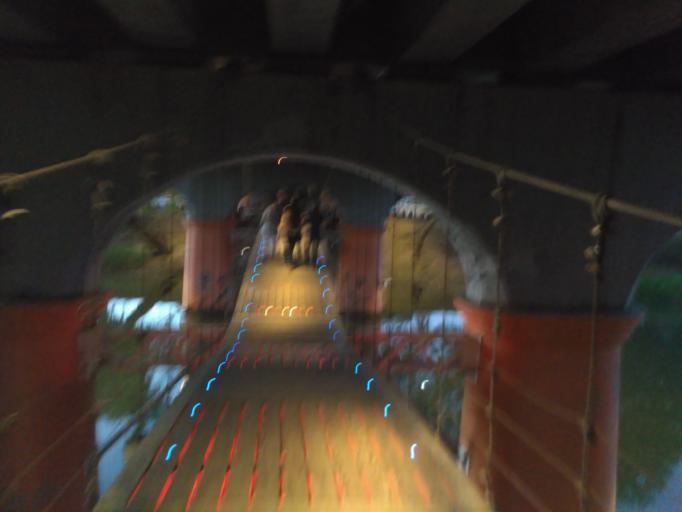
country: MX
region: Sinaloa
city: Culiacan
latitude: 24.8123
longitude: -107.4025
